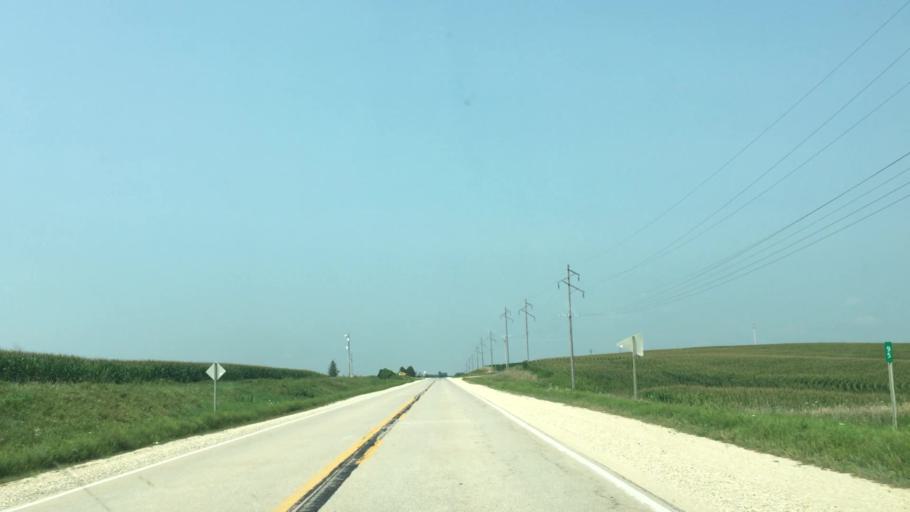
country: US
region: Iowa
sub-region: Winneshiek County
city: Decorah
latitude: 43.1451
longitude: -91.8642
